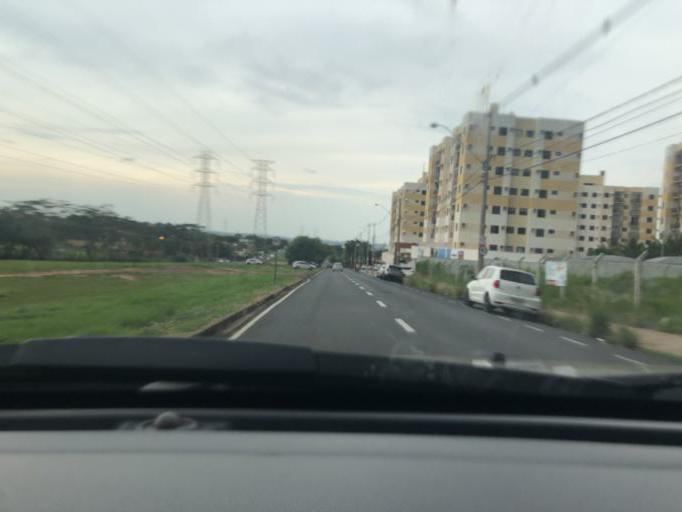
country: BR
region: Sao Paulo
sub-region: Sao Jose Do Rio Preto
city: Sao Jose do Rio Preto
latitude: -20.8445
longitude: -49.3874
